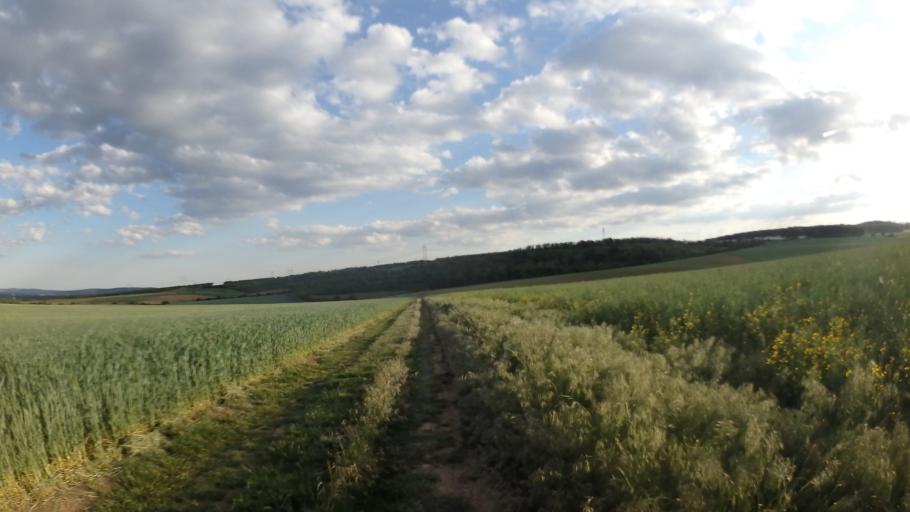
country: CZ
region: South Moravian
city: Moravany
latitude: 49.1373
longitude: 16.5905
